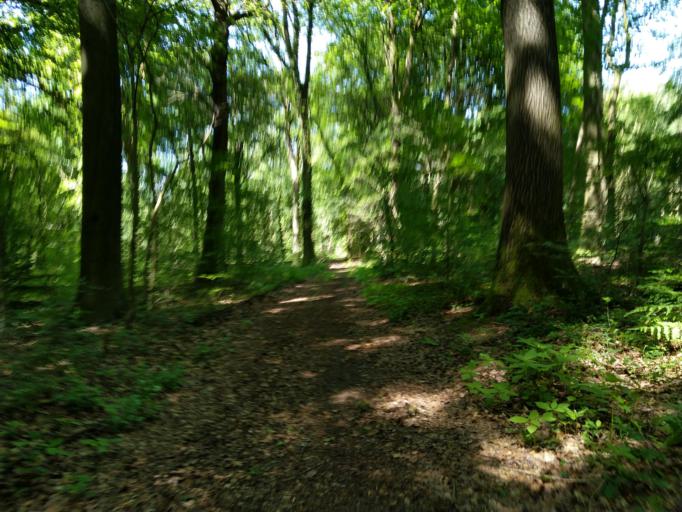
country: BE
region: Wallonia
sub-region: Province du Hainaut
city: Jurbise
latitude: 50.4964
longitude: 3.9123
